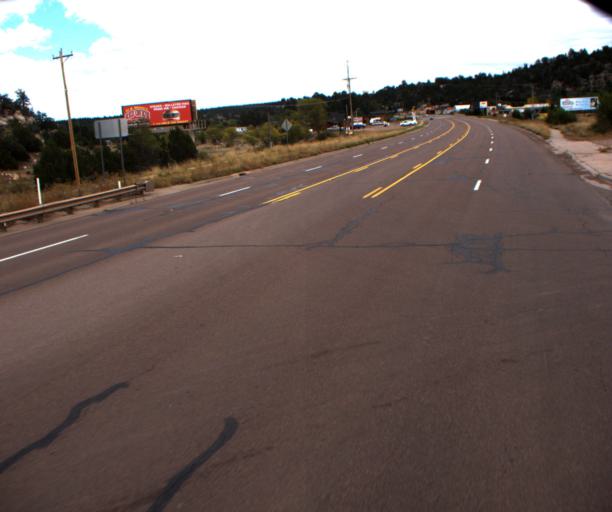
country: US
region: Arizona
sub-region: Navajo County
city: Heber-Overgaard
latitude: 34.4313
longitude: -110.5983
